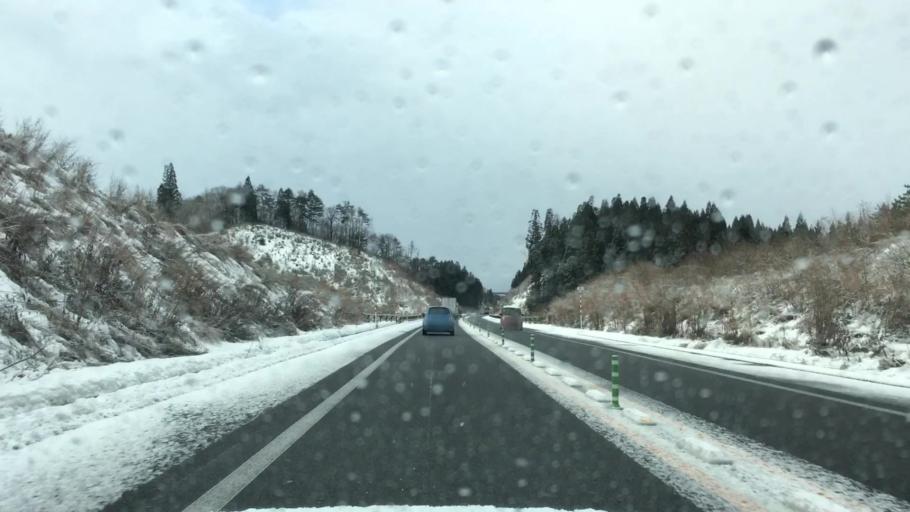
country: JP
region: Akita
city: Takanosu
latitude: 40.2111
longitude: 140.4156
